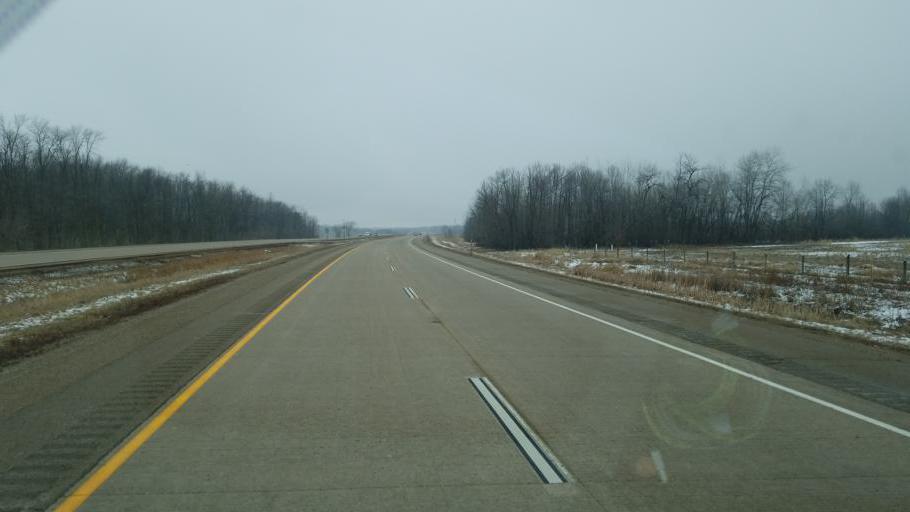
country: US
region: Wisconsin
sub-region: Winnebago County
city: Winneconne
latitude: 44.2359
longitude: -88.7798
